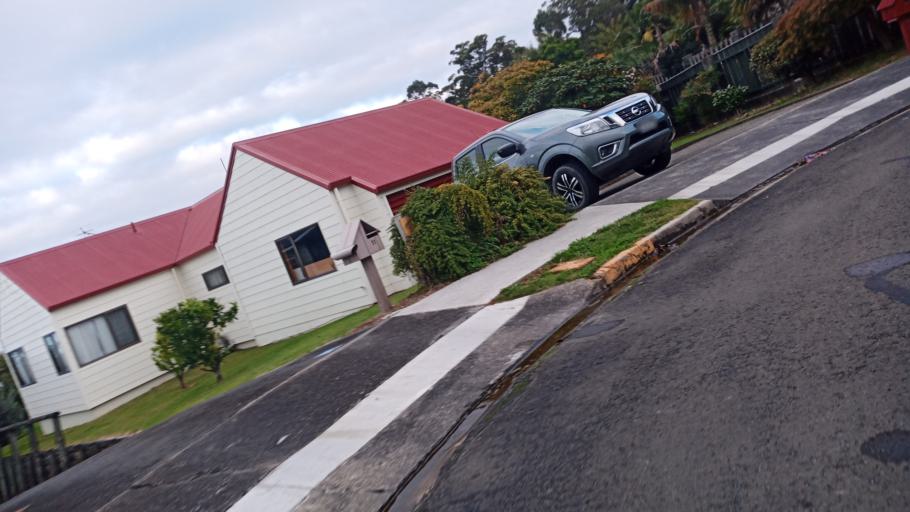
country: NZ
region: Gisborne
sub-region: Gisborne District
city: Gisborne
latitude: -38.6495
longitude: 178.0293
